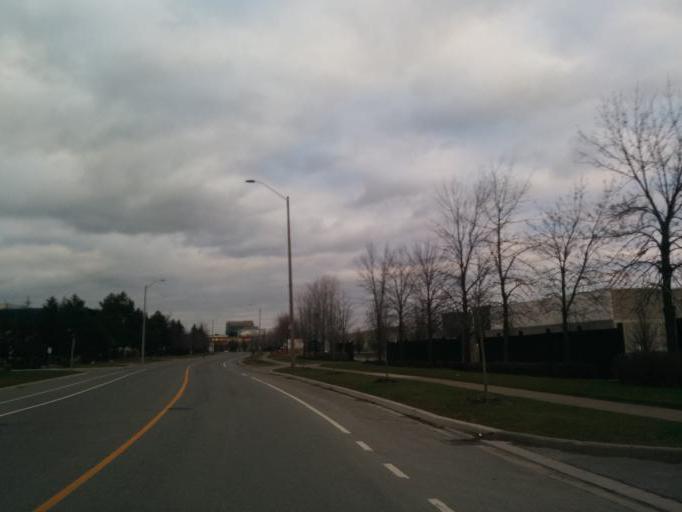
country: CA
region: Ontario
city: Etobicoke
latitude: 43.6535
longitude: -79.6043
